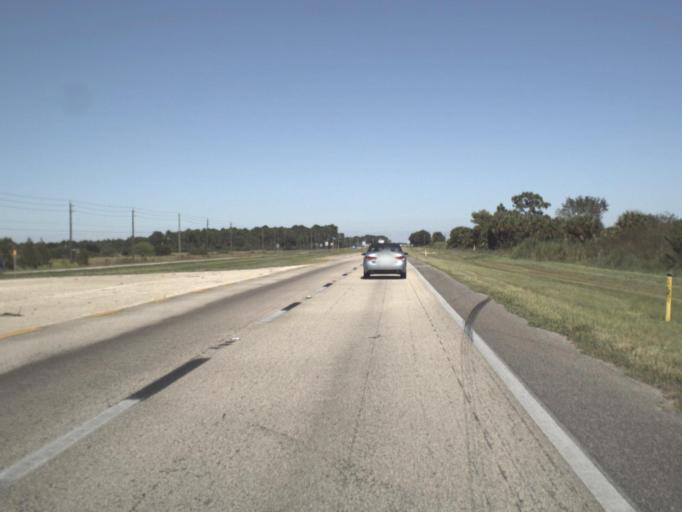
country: US
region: Florida
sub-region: Hendry County
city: LaBelle
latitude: 26.7142
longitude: -81.5028
